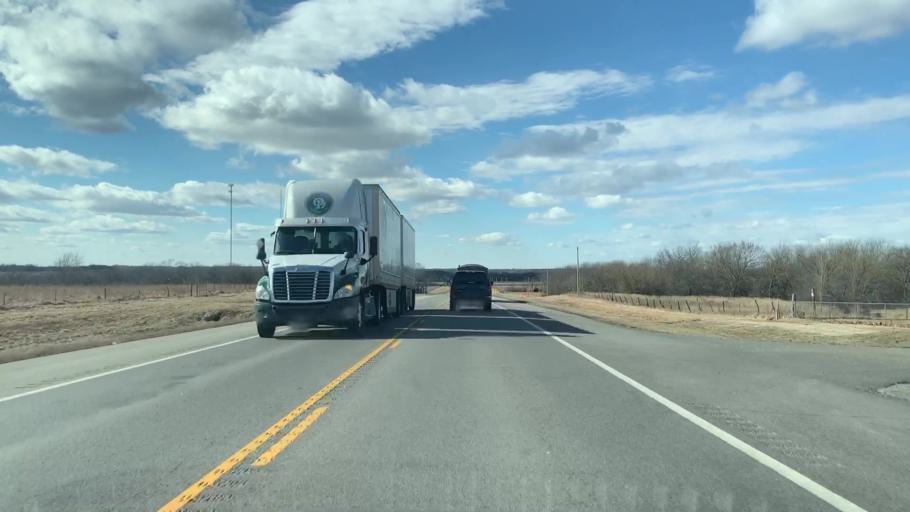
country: US
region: Kansas
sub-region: Cherokee County
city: Columbus
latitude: 37.3400
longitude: -94.9088
